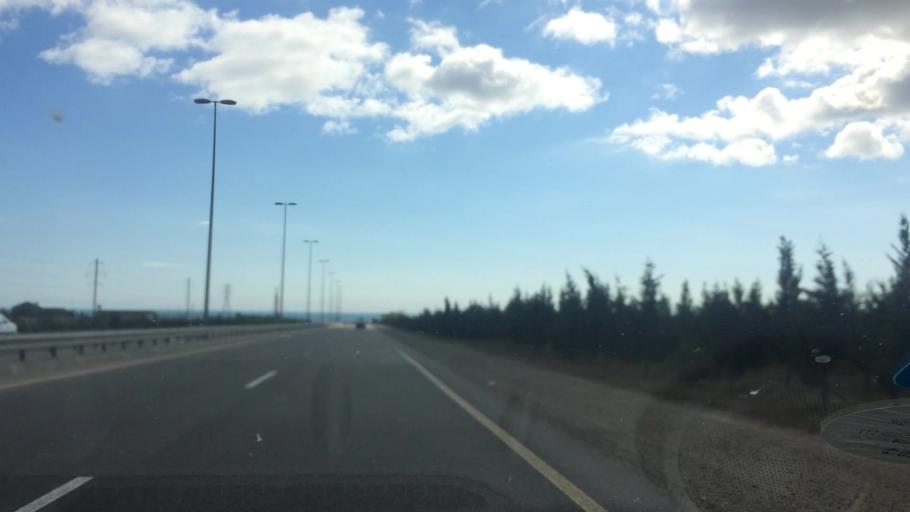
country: AZ
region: Baki
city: Zyrya
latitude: 40.4032
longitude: 50.3059
